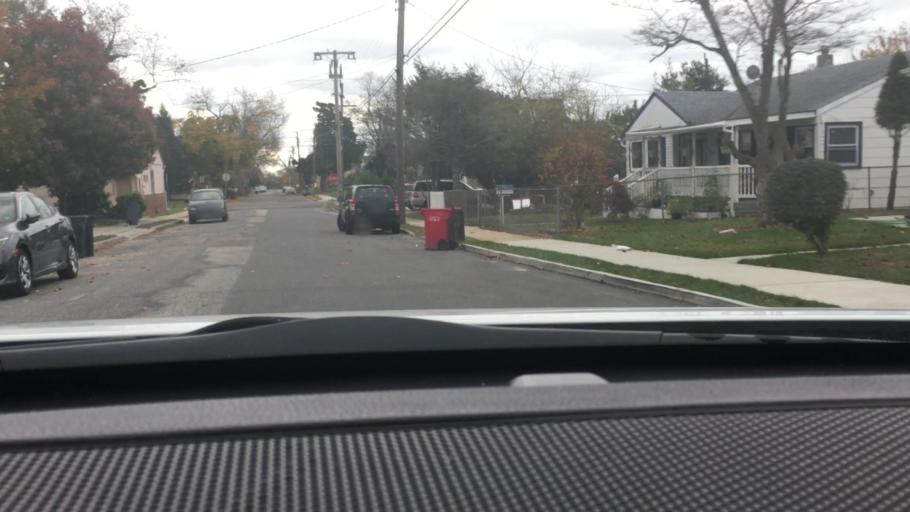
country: US
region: New Jersey
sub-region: Atlantic County
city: Northfield
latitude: 39.3784
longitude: -74.5368
